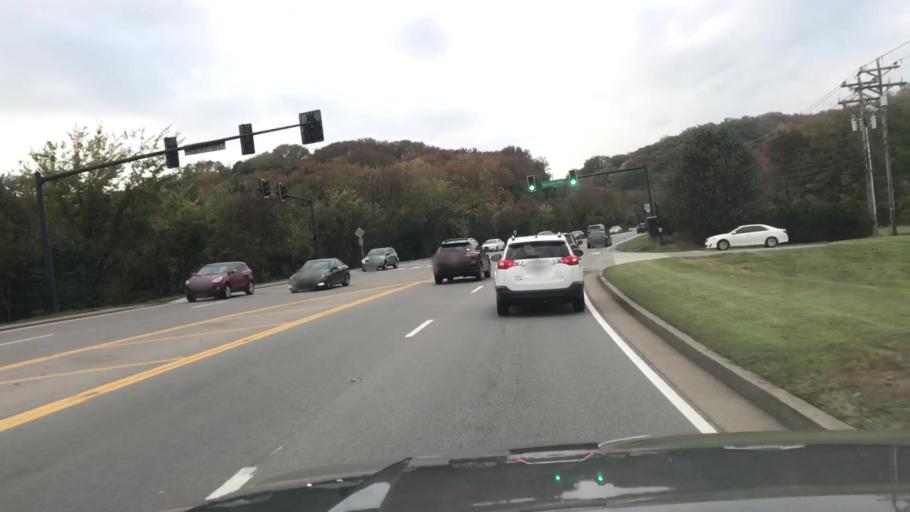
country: US
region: Tennessee
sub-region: Williamson County
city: Franklin
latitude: 35.9682
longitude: -86.8186
